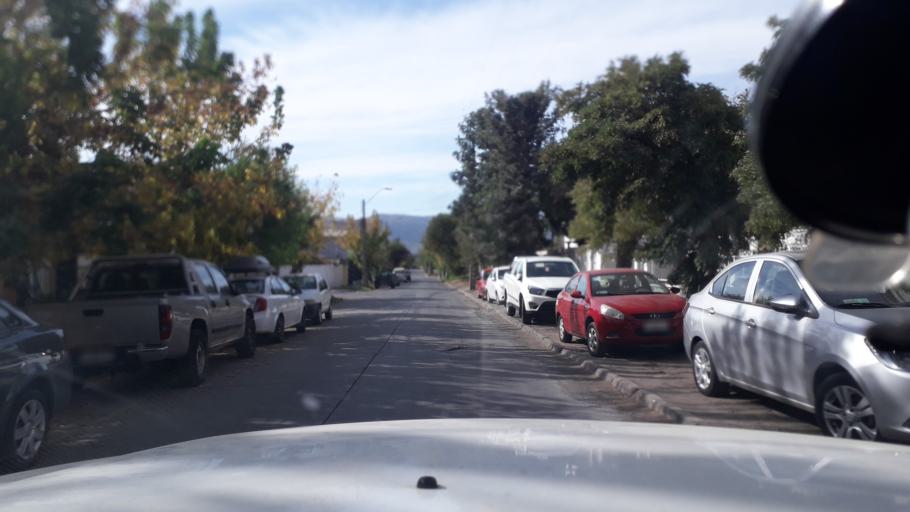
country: CL
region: Valparaiso
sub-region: Provincia de San Felipe
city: San Felipe
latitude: -32.7540
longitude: -70.7164
